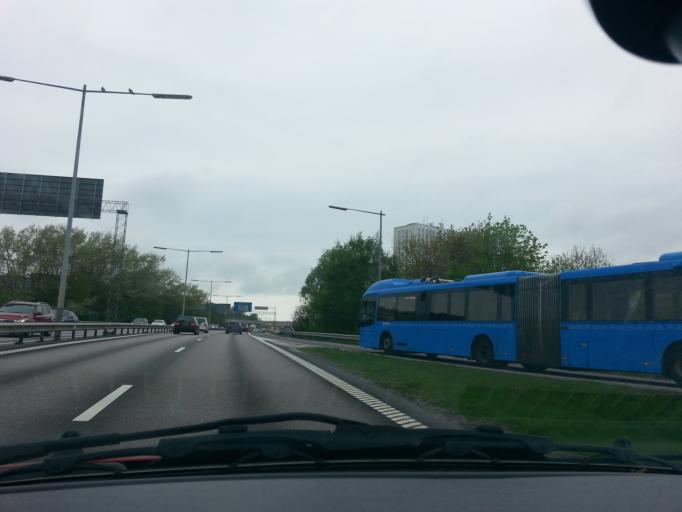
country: SE
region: Vaestra Goetaland
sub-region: Goteborg
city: Majorna
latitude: 57.6483
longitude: 11.9152
